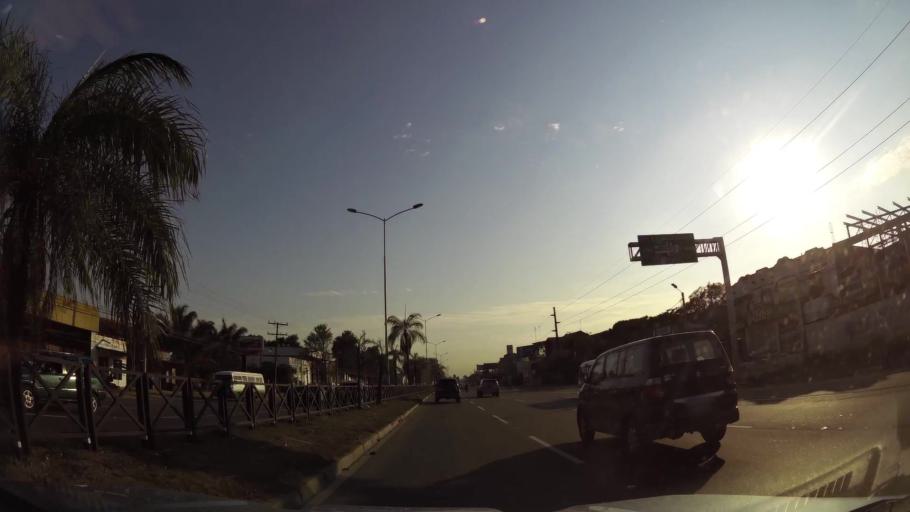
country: BO
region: Santa Cruz
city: Santa Cruz de la Sierra
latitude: -17.7355
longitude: -63.1696
